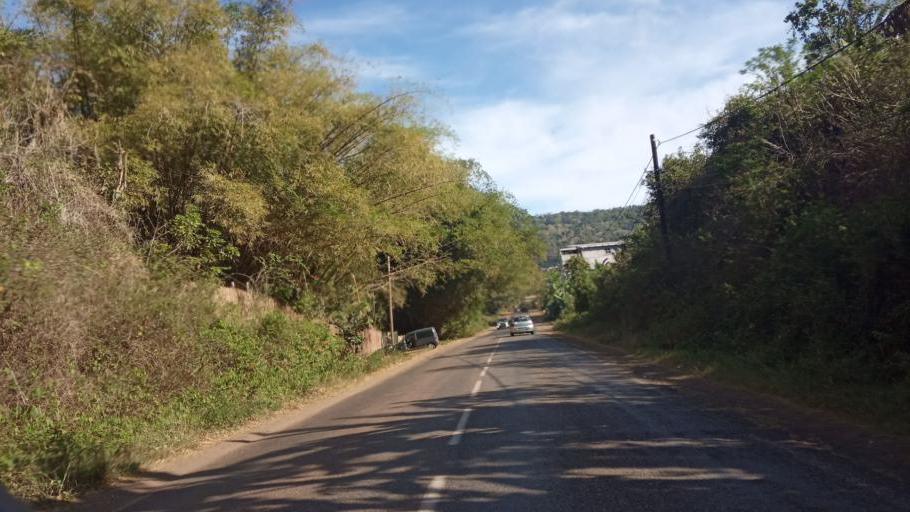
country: YT
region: Dembeni
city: Dembeni
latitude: -12.8637
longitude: 45.1982
